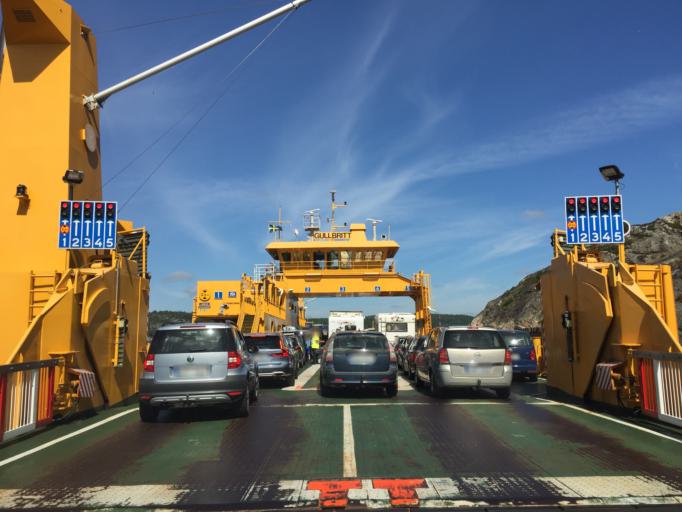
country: SE
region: Vaestra Goetaland
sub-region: Lysekils Kommun
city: Brastad
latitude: 58.3002
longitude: 11.5349
